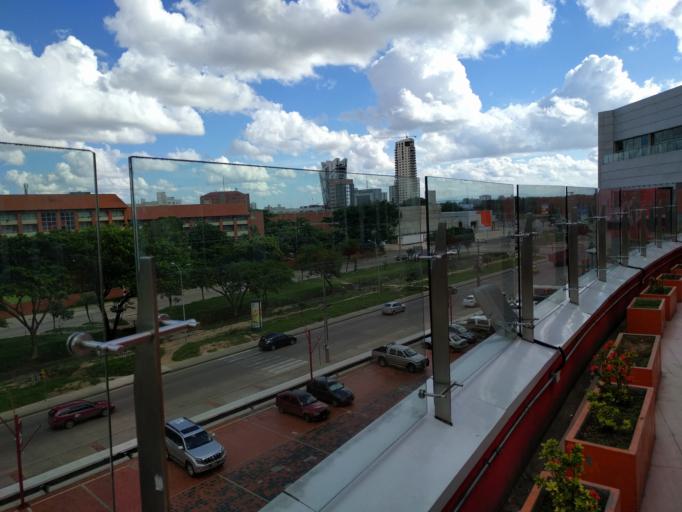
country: BO
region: Santa Cruz
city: Santa Cruz de la Sierra
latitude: -17.7546
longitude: -63.1992
